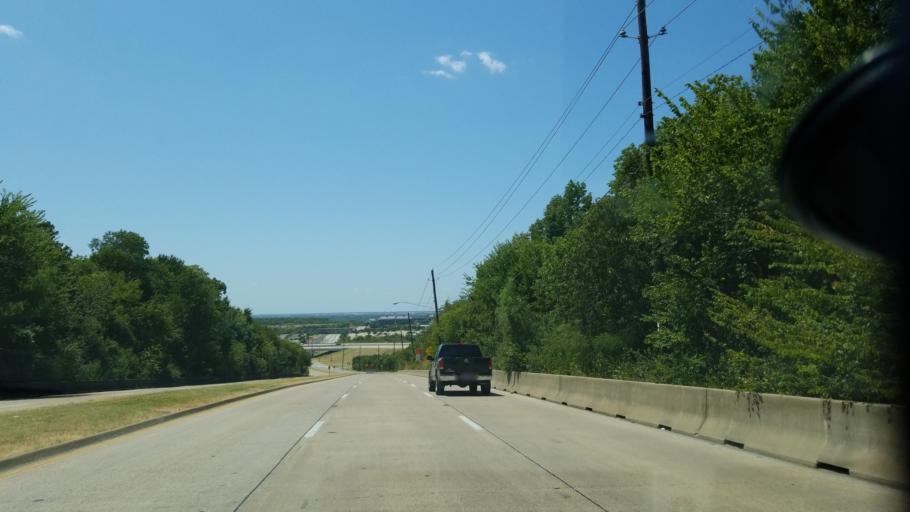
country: US
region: Texas
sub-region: Dallas County
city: Cockrell Hill
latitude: 32.7063
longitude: -96.9278
